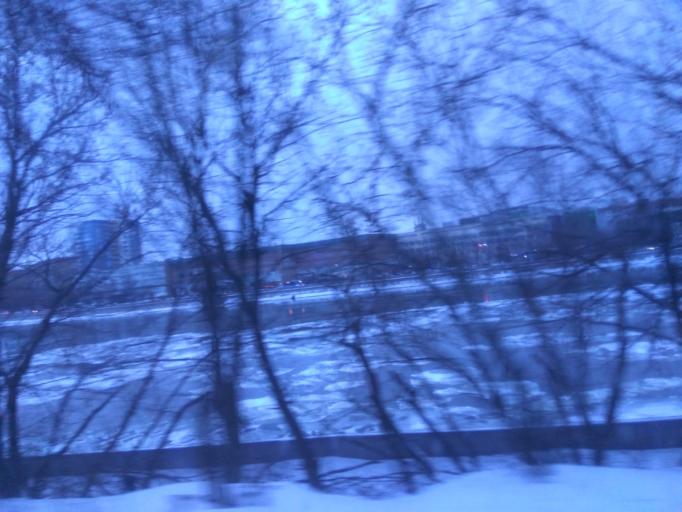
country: RU
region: Moscow
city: Taganskiy
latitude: 55.7229
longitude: 37.6592
